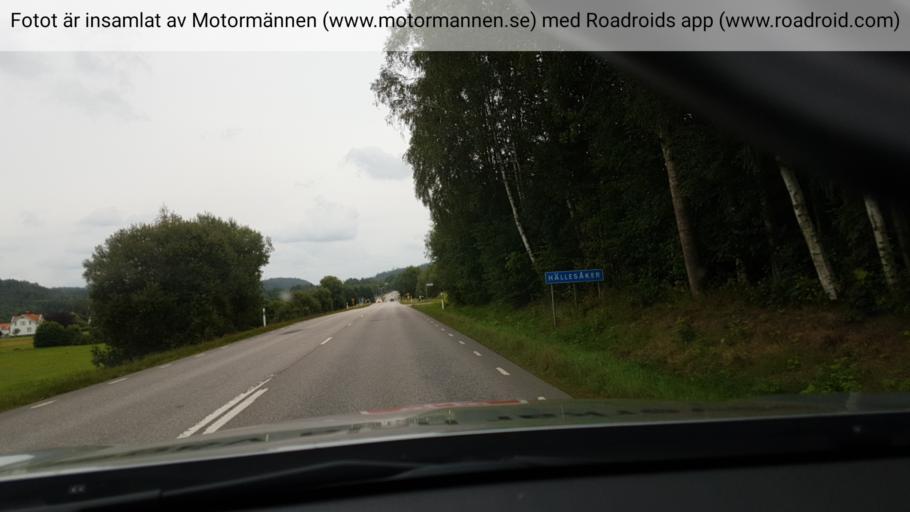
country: SE
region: Vaestra Goetaland
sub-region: Harryda Kommun
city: Molnlycke
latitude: 57.5999
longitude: 12.1721
